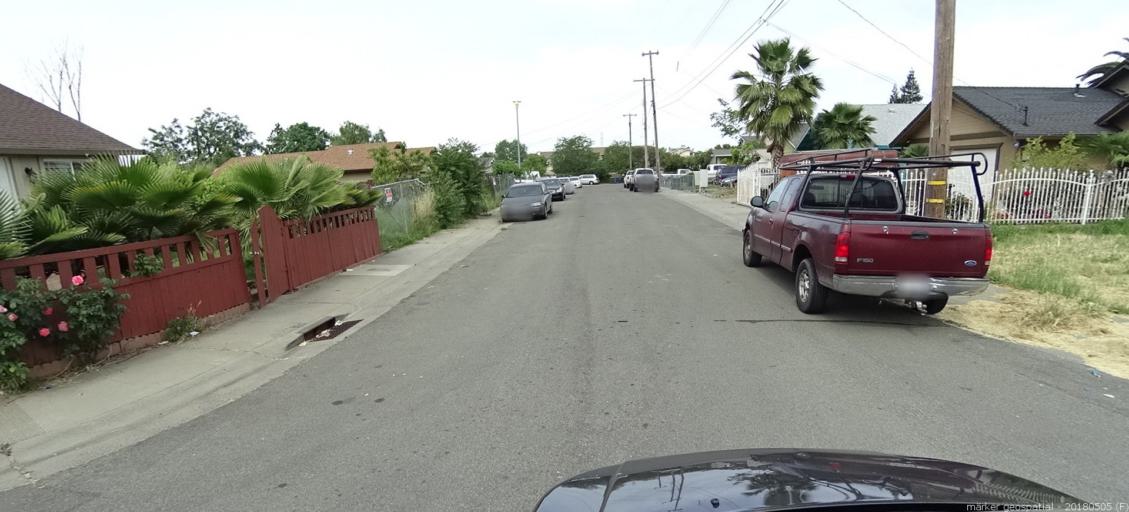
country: US
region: California
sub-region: Sacramento County
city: Rio Linda
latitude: 38.6409
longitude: -121.4408
